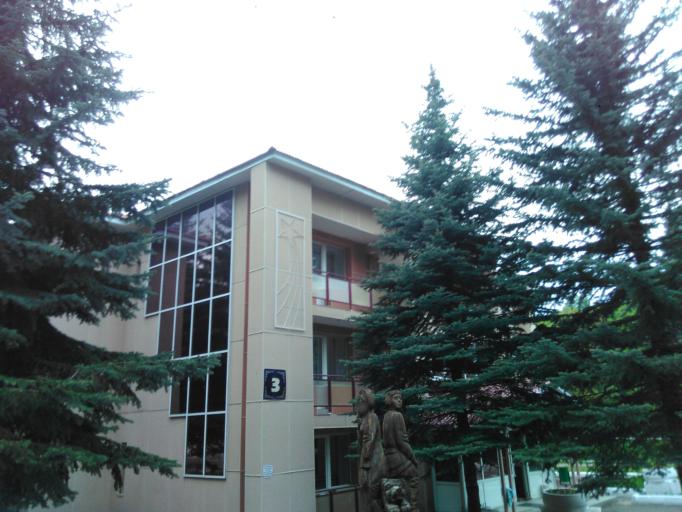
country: RU
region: Tatarstan
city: Al'met'yevsk
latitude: 54.9525
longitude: 52.2654
